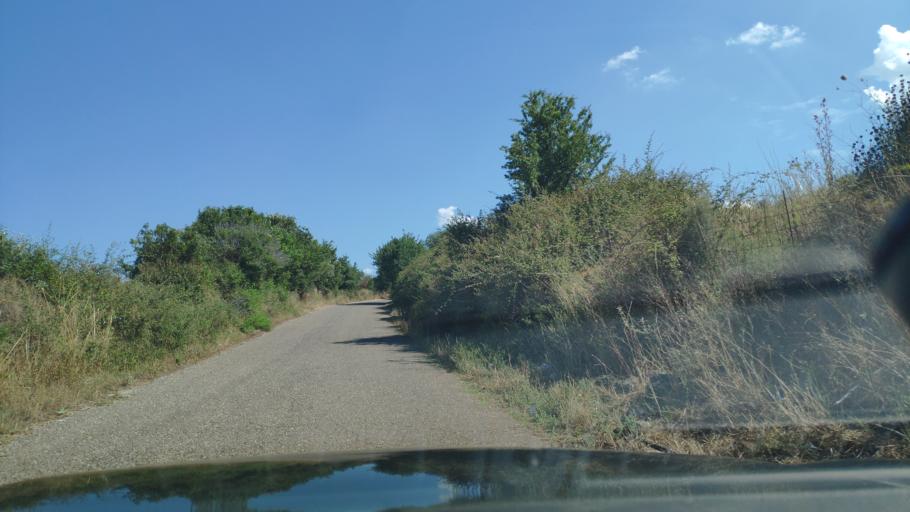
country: GR
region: West Greece
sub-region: Nomos Aitolias kai Akarnanias
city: Katouna
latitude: 38.8141
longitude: 21.1055
